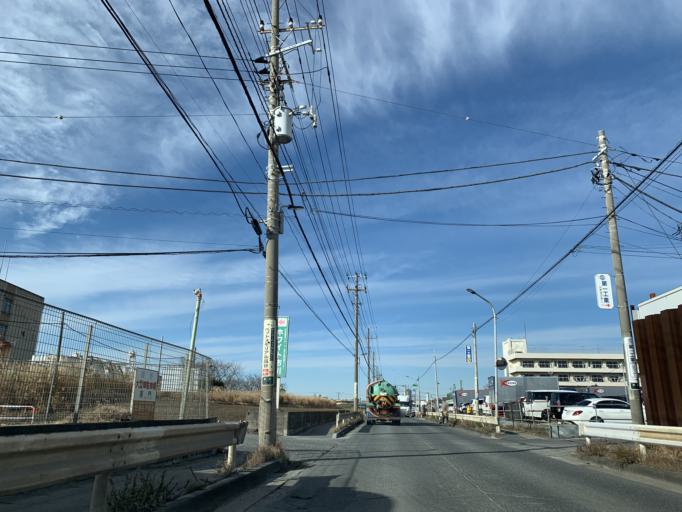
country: JP
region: Chiba
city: Funabashi
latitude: 35.6931
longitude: 139.9454
